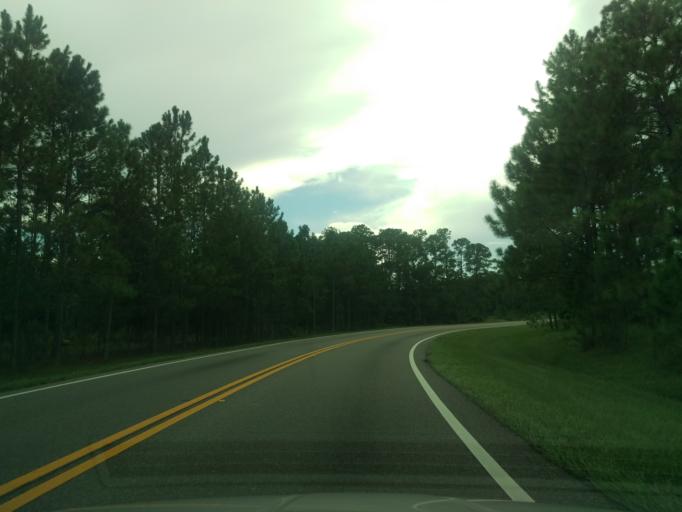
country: US
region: Florida
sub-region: Osceola County
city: Celebration
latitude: 28.3912
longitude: -81.5604
